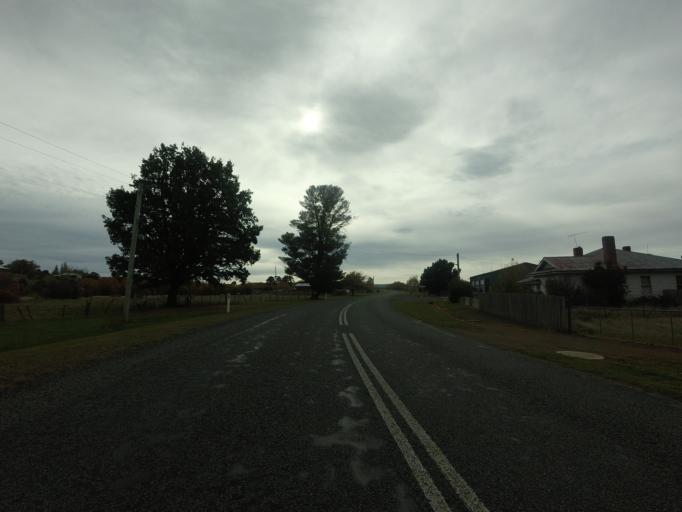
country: AU
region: Tasmania
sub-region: Derwent Valley
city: New Norfolk
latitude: -42.3828
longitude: 147.0030
